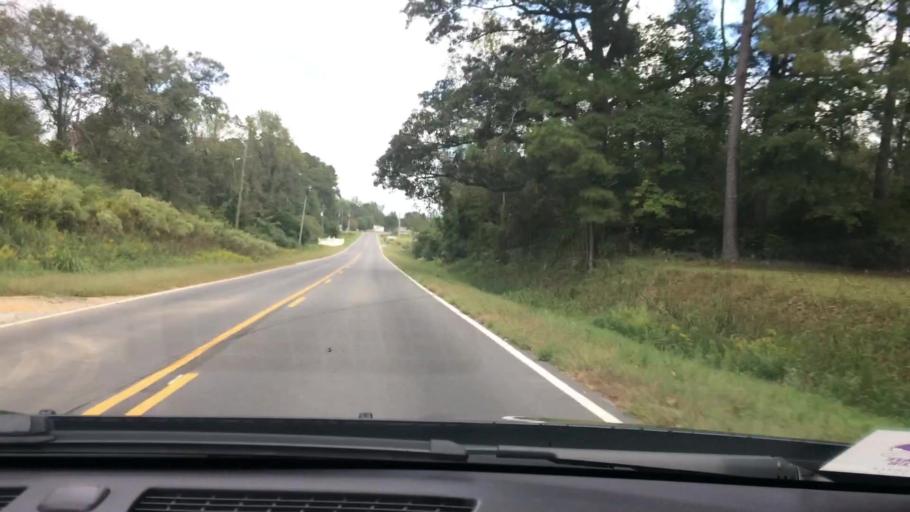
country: US
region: North Carolina
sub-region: Pitt County
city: Ayden
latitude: 35.4608
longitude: -77.4669
